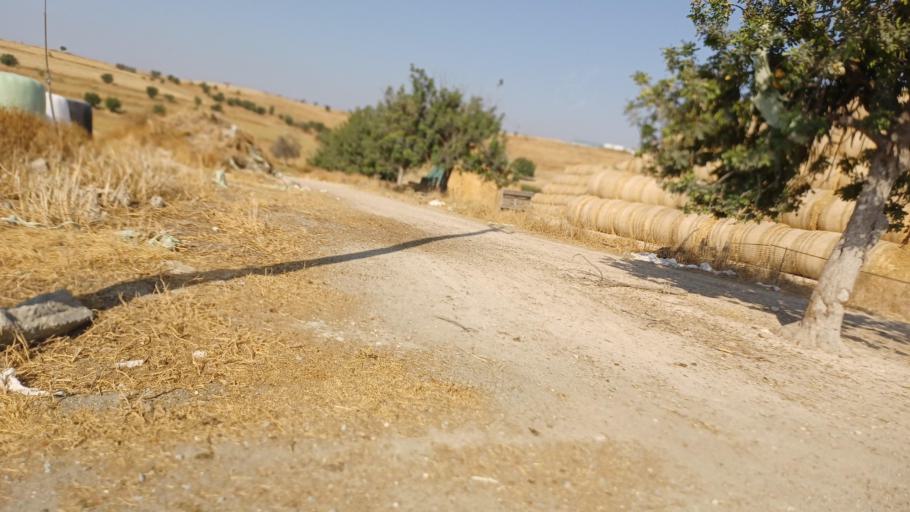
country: CY
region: Lefkosia
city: Lympia
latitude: 34.9868
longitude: 33.4677
